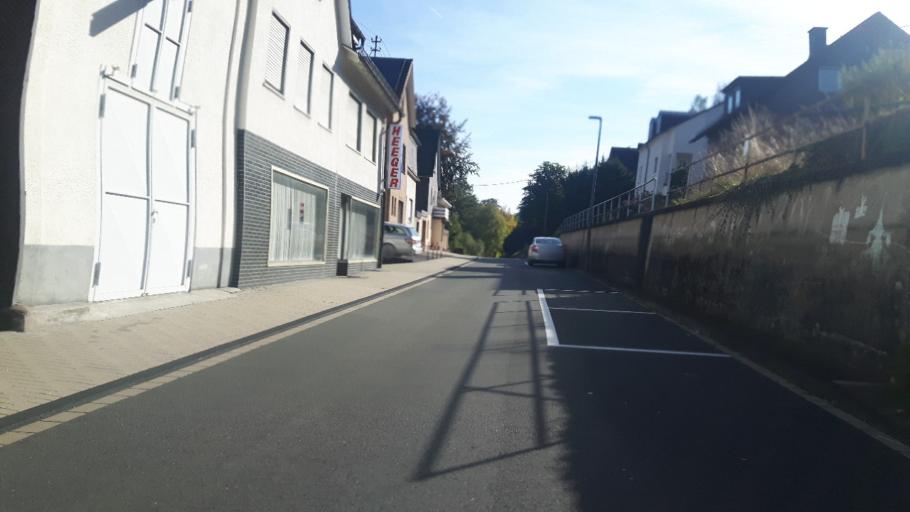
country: DE
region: North Rhine-Westphalia
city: Netphen
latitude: 50.9115
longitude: 8.0572
